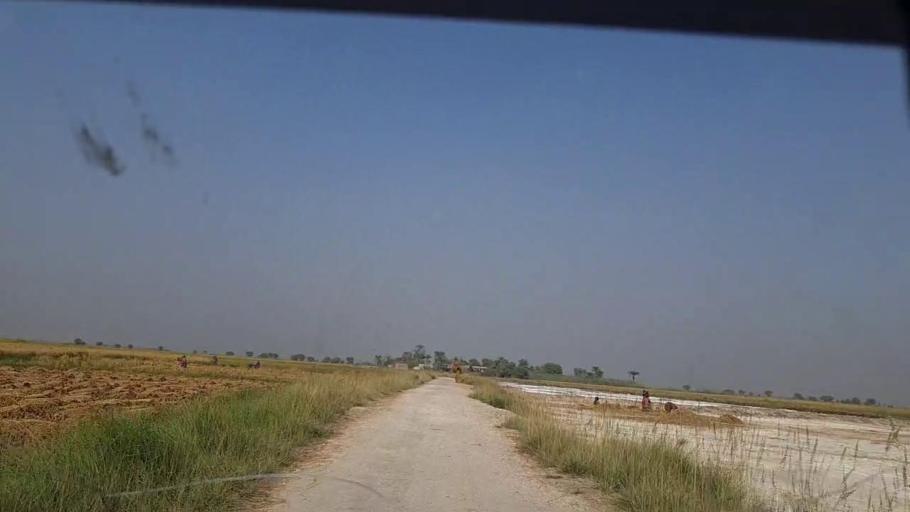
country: PK
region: Sindh
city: Shikarpur
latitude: 28.0922
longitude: 68.5995
